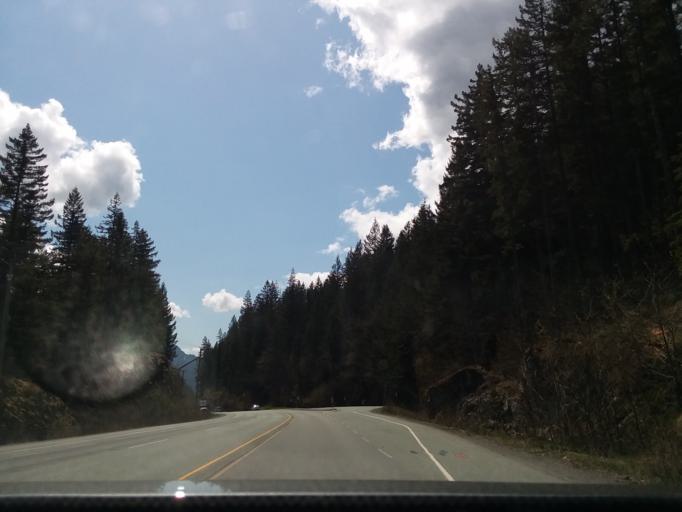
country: CA
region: British Columbia
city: Whistler
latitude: 50.0204
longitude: -123.1225
